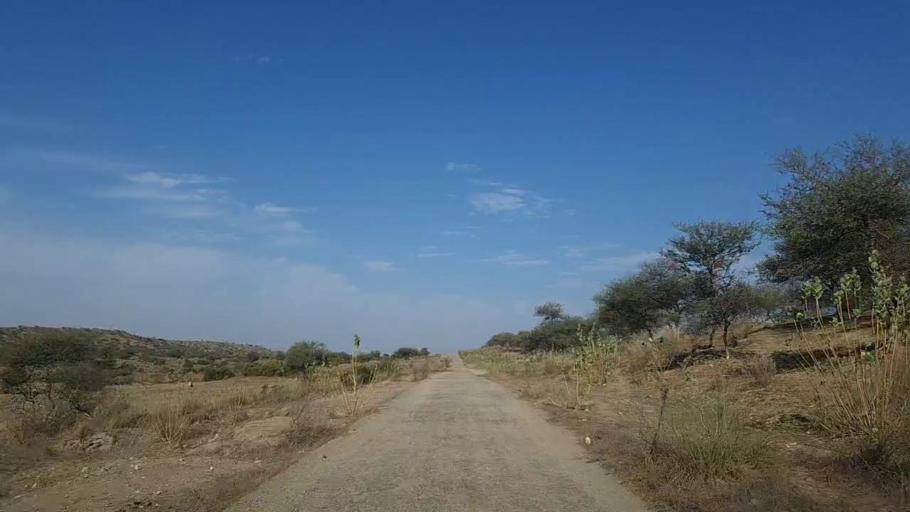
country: PK
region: Sindh
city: Naukot
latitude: 24.8499
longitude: 69.5358
